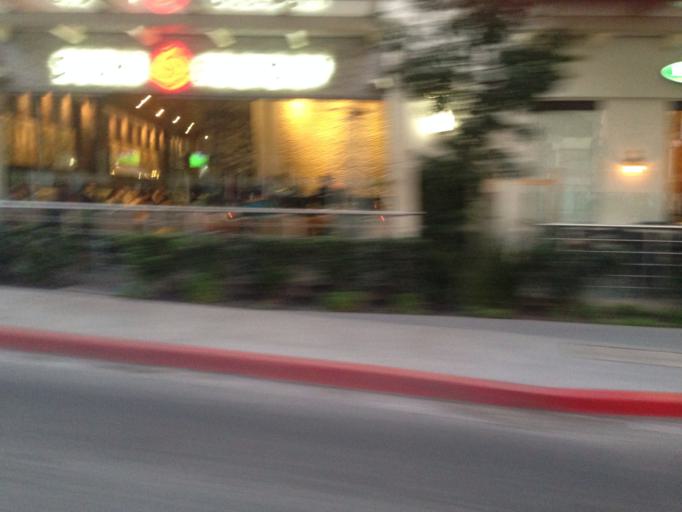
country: MX
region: Baja California
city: Tijuana
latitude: 32.5136
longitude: -117.0119
